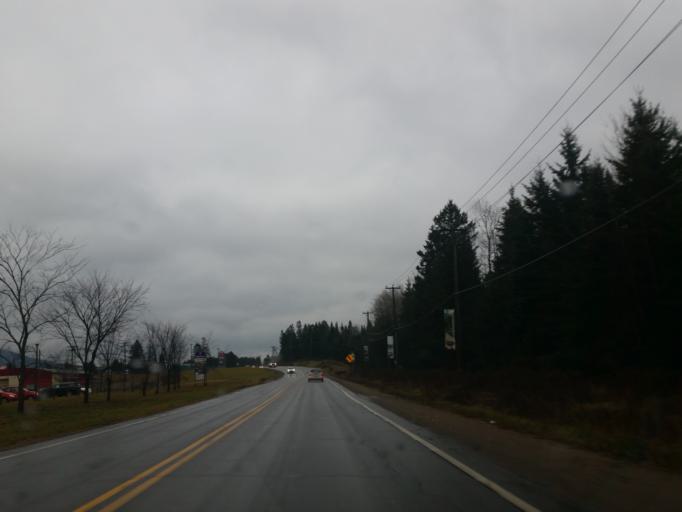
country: CA
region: Quebec
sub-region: Capitale-Nationale
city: Shannon
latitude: 46.8868
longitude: -71.5079
